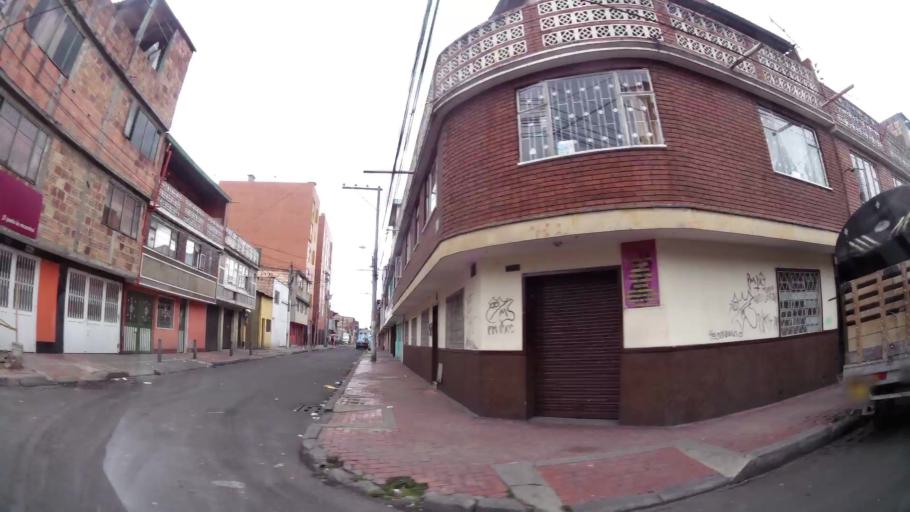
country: CO
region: Bogota D.C.
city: Bogota
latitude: 4.6754
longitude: -74.0986
